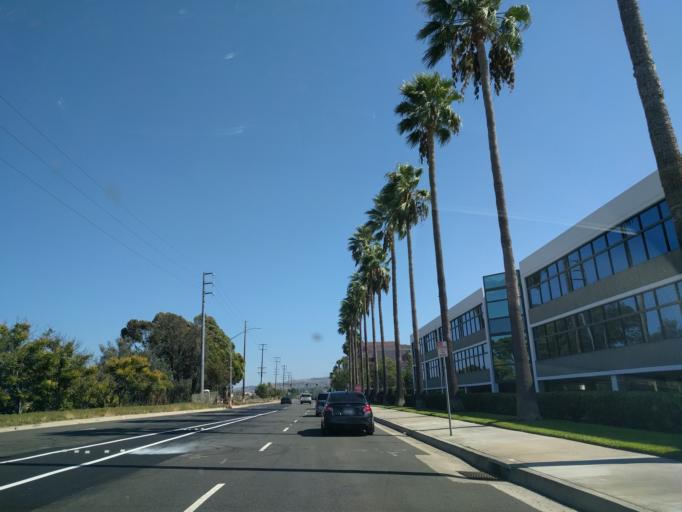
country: US
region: California
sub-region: Orange County
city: Irvine
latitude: 33.6580
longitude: -117.8699
